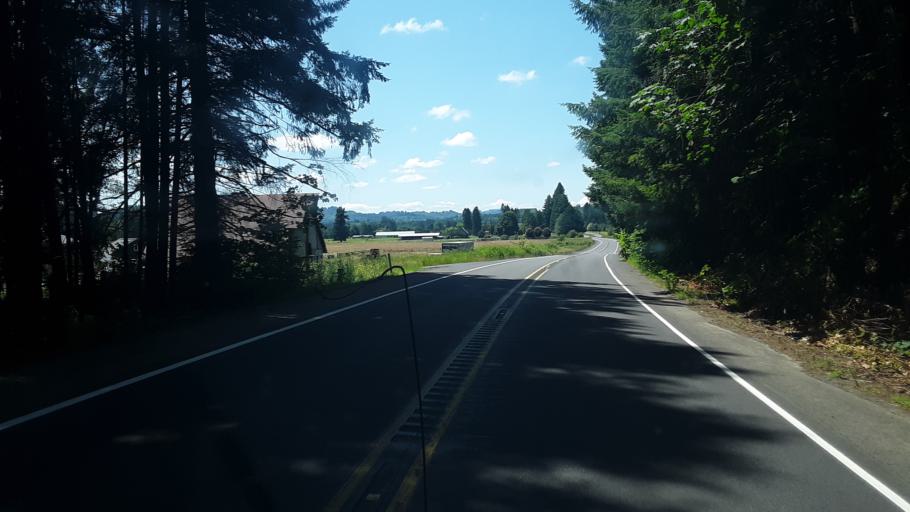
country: US
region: Washington
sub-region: Clark County
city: Amboy
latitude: 45.9239
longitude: -122.3935
